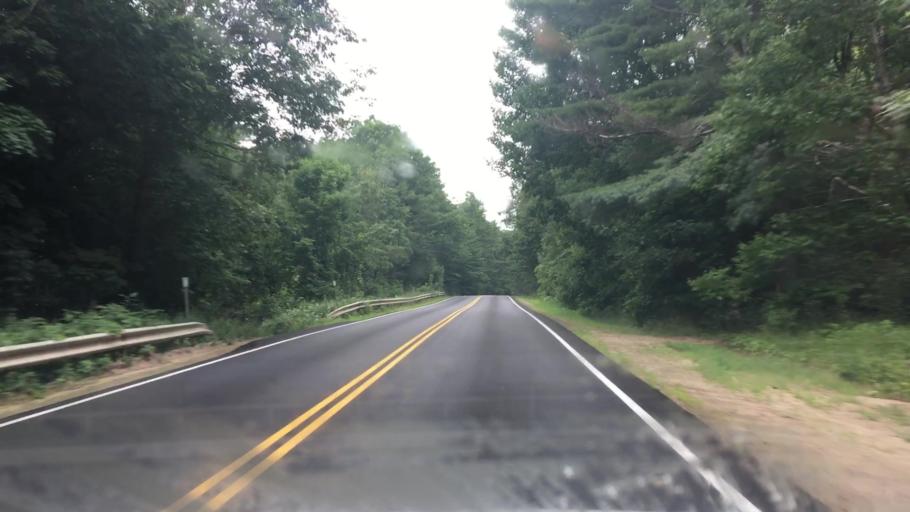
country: US
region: New York
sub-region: Clinton County
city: Morrisonville
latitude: 44.6230
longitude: -73.6021
